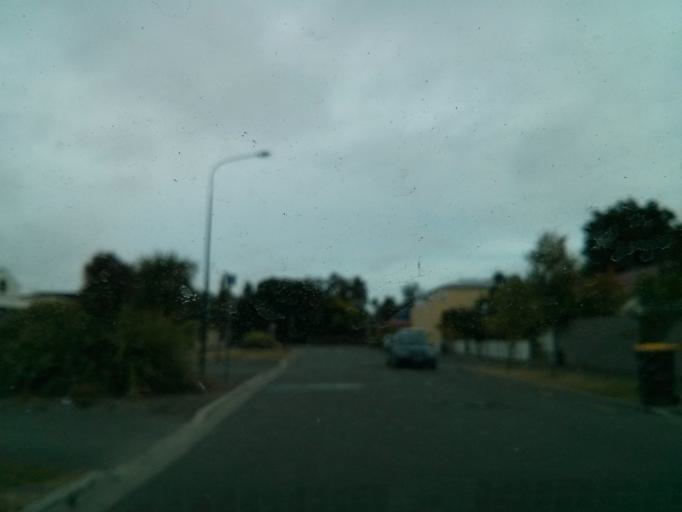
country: NZ
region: Canterbury
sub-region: Christchurch City
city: Christchurch
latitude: -43.5311
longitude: 172.5932
